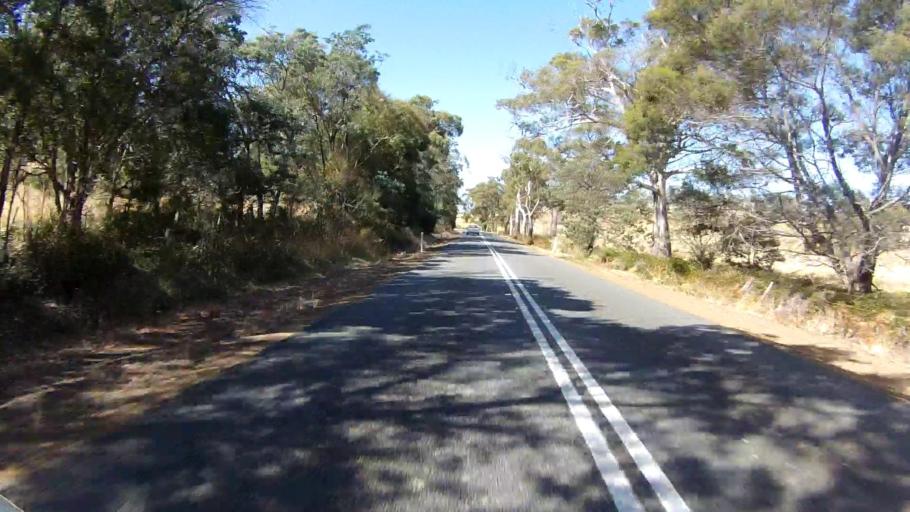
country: AU
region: Tasmania
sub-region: Sorell
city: Sorell
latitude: -42.3013
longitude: 147.9768
